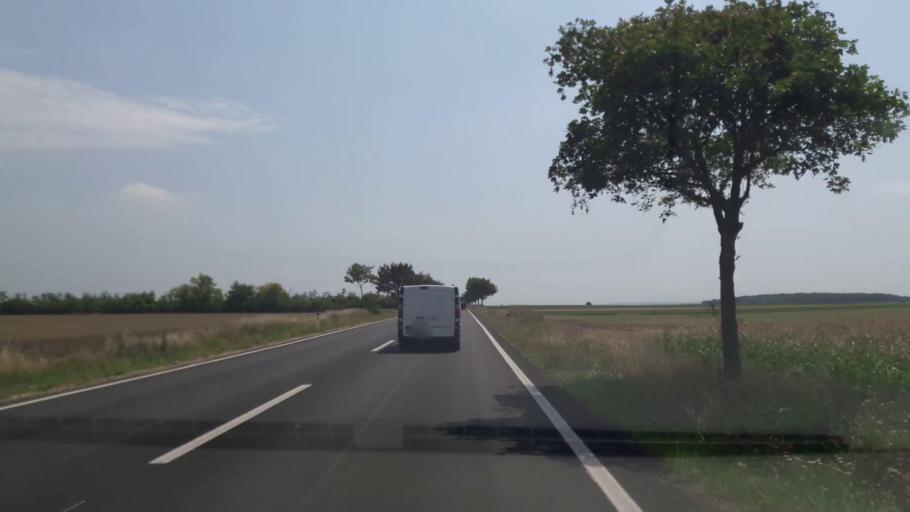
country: AT
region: Lower Austria
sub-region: Politischer Bezirk Wien-Umgebung
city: Rauchenwarth
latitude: 48.0963
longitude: 16.5435
